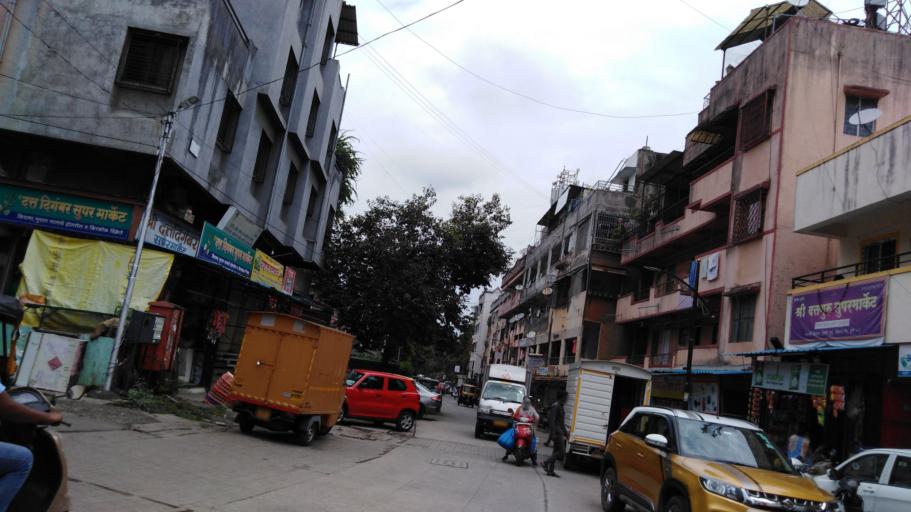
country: IN
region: Maharashtra
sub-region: Pune Division
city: Pune
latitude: 18.4798
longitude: 73.8280
